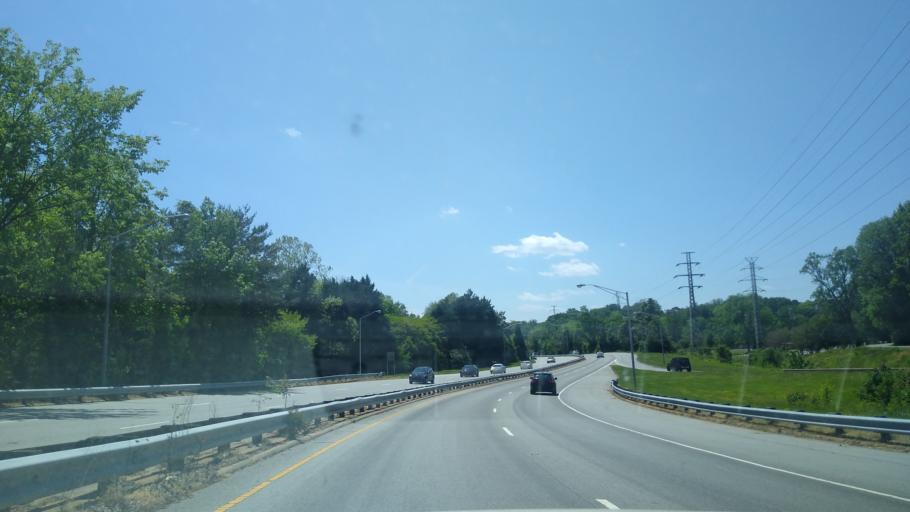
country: US
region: North Carolina
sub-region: Guilford County
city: Greensboro
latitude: 36.0739
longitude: -79.8328
